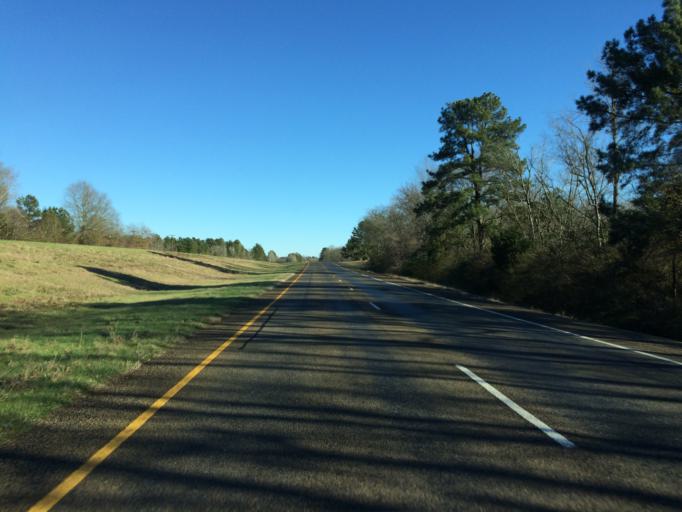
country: US
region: Texas
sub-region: Wood County
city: Hawkins
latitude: 32.5923
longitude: -95.2284
